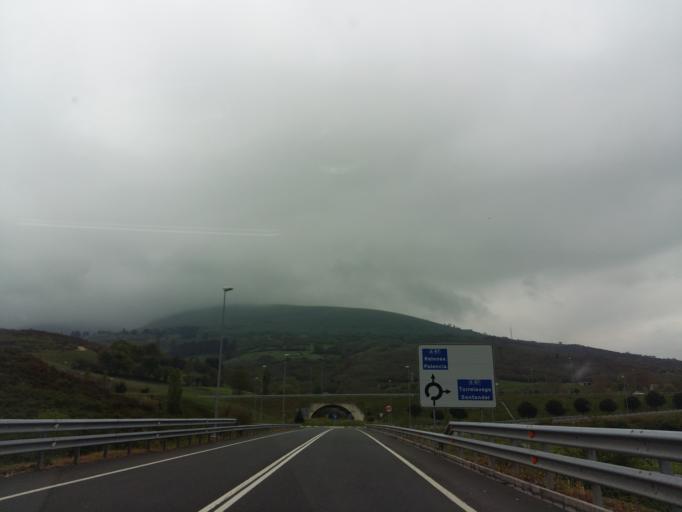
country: ES
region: Cantabria
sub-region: Provincia de Cantabria
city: Arenas de Iguna
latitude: 43.1856
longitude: -4.0577
